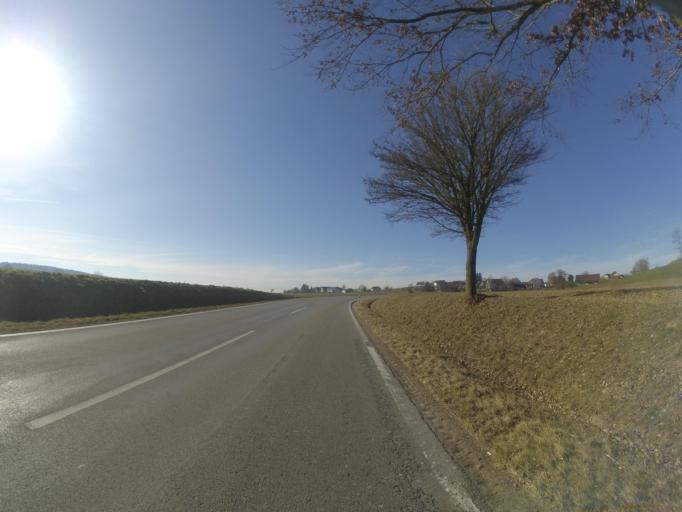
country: DE
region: Baden-Wuerttemberg
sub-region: Tuebingen Region
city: Wolpertswende
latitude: 47.9213
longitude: 9.6298
